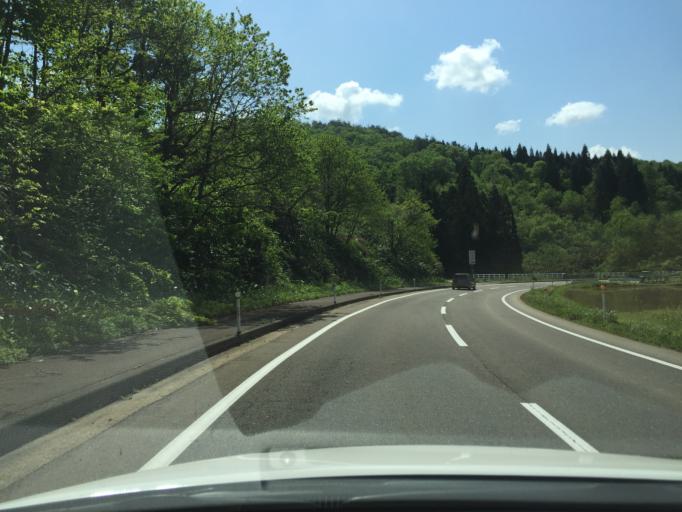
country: JP
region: Niigata
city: Kamo
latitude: 37.5907
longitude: 139.0942
